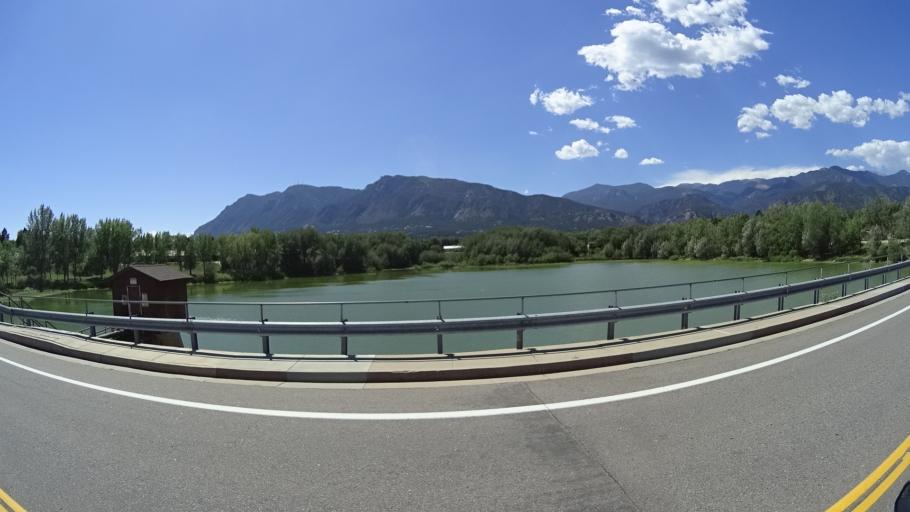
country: US
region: Colorado
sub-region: El Paso County
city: Colorado Springs
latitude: 38.7944
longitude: -104.8289
